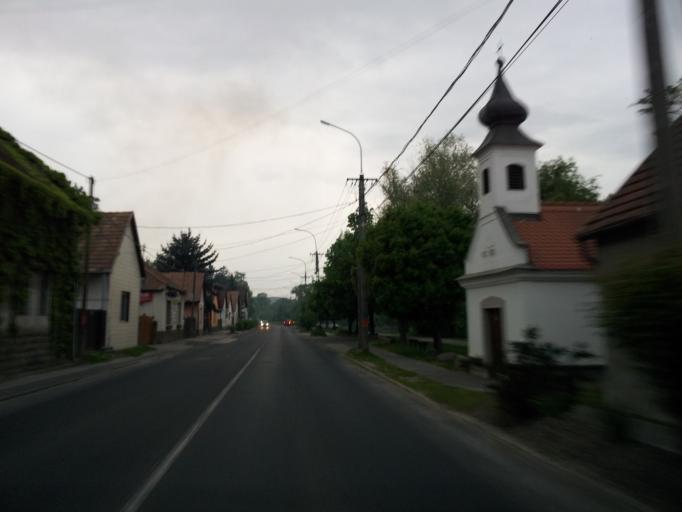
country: HU
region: Pest
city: Dunabogdany
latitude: 47.7976
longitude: 19.0267
